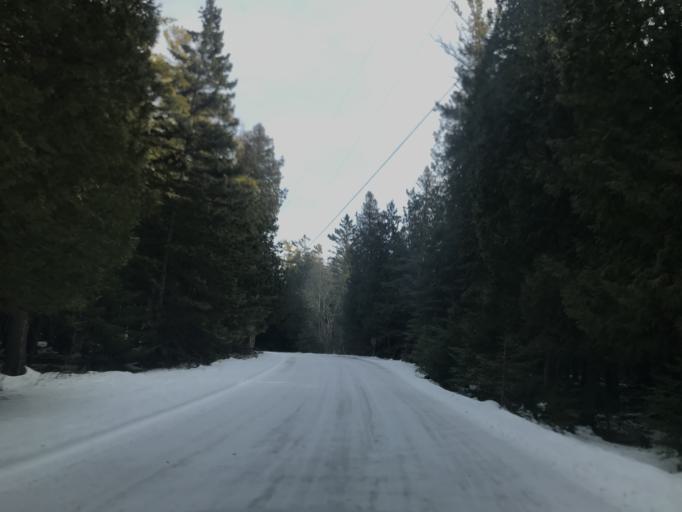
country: US
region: Wisconsin
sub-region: Door County
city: Sturgeon Bay
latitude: 45.1412
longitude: -87.0503
